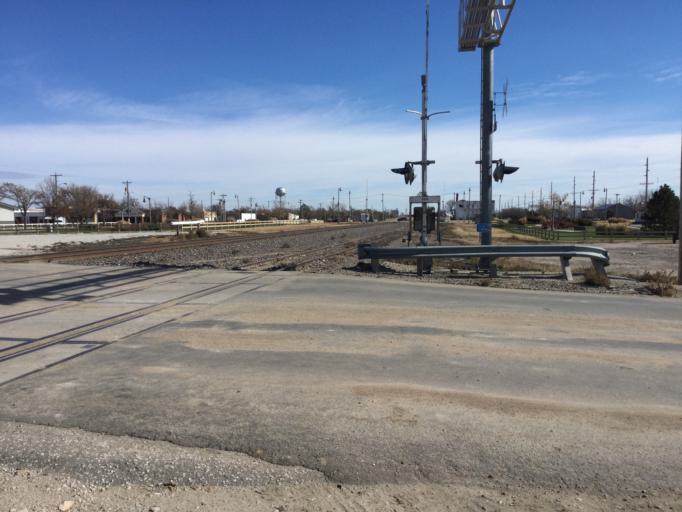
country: US
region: Kansas
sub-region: Trego County
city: WaKeeney
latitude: 39.0234
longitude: -99.8856
